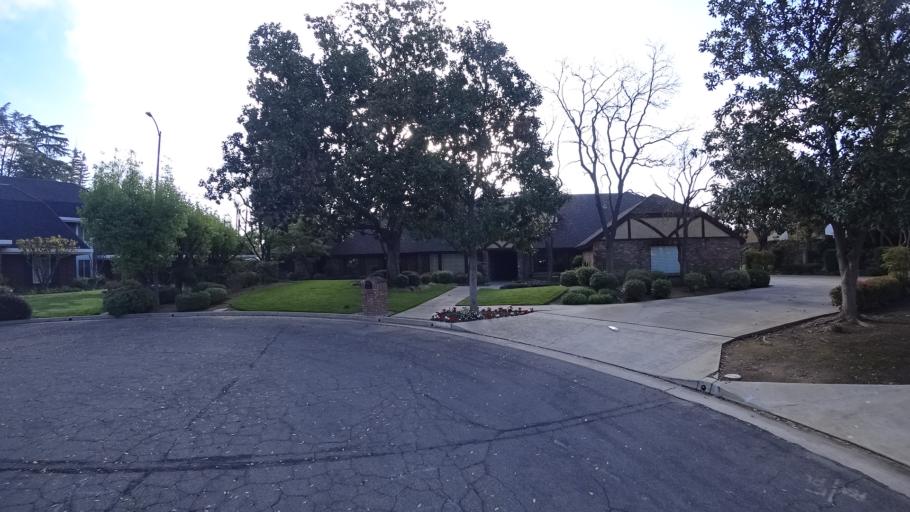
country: US
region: California
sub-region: Fresno County
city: Fresno
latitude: 36.8141
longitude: -119.8292
